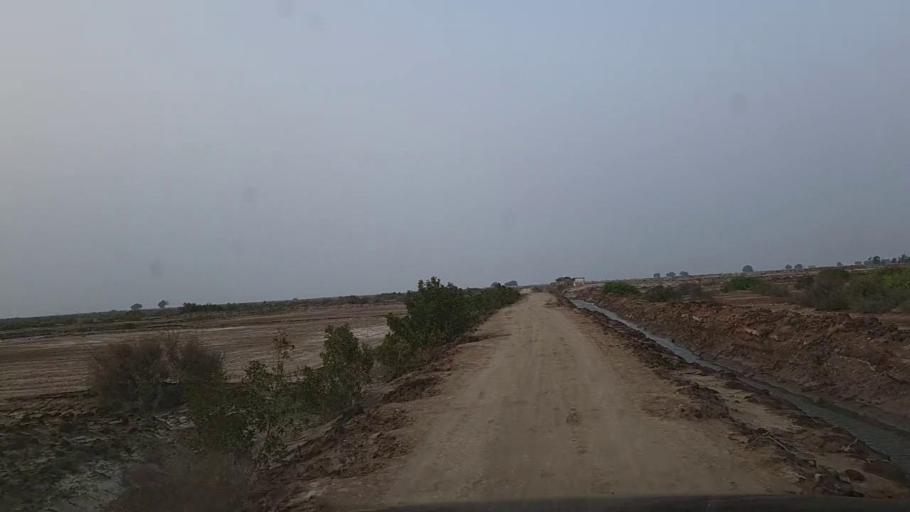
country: PK
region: Sindh
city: Gharo
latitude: 24.7451
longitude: 67.7204
